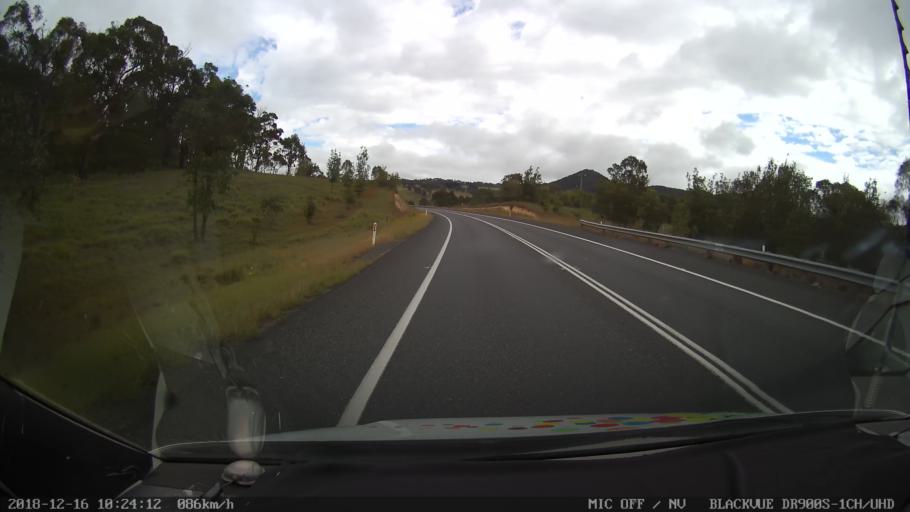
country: AU
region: New South Wales
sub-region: Tenterfield Municipality
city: Carrolls Creek
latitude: -29.1734
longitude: 152.0072
